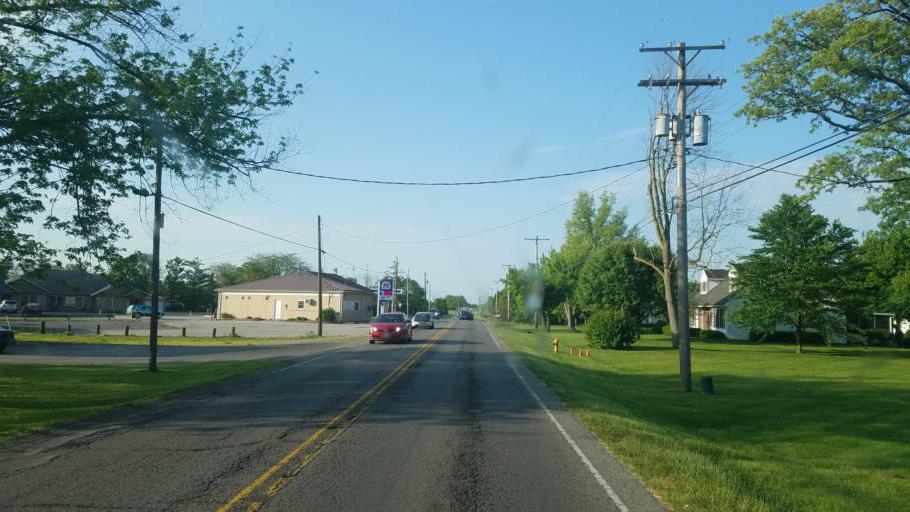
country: US
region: Ohio
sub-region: Fayette County
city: Washington Court House
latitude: 39.5245
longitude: -83.4431
